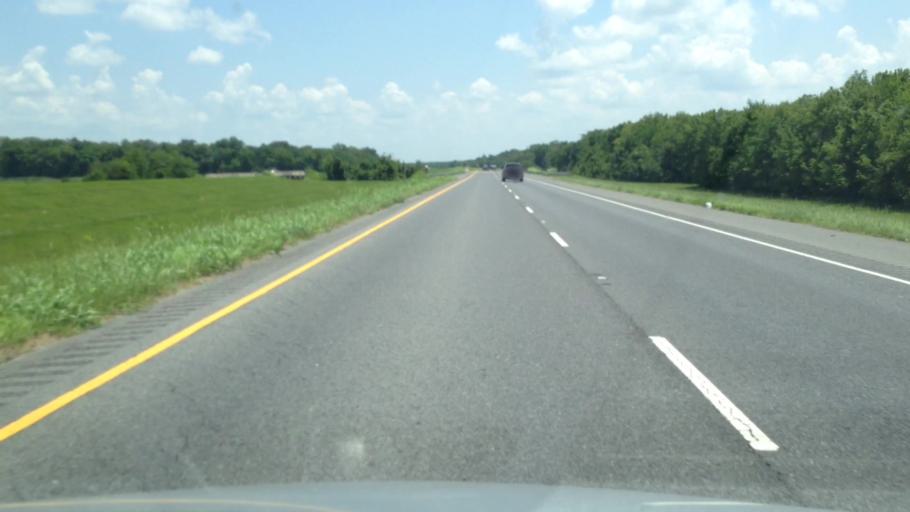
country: US
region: Louisiana
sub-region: Avoyelles Parish
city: Bunkie
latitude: 30.8231
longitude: -92.2237
